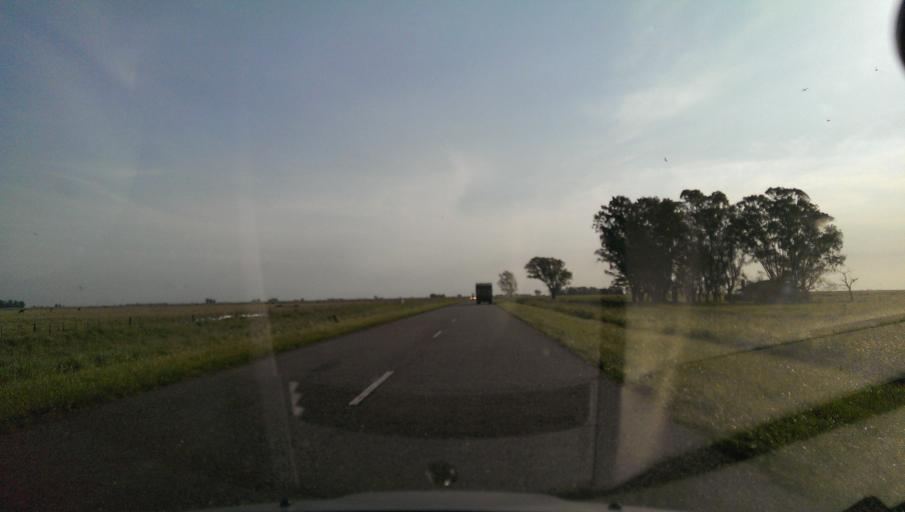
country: AR
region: Buenos Aires
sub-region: Partido de General La Madrid
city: General La Madrid
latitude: -37.4675
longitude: -61.1480
